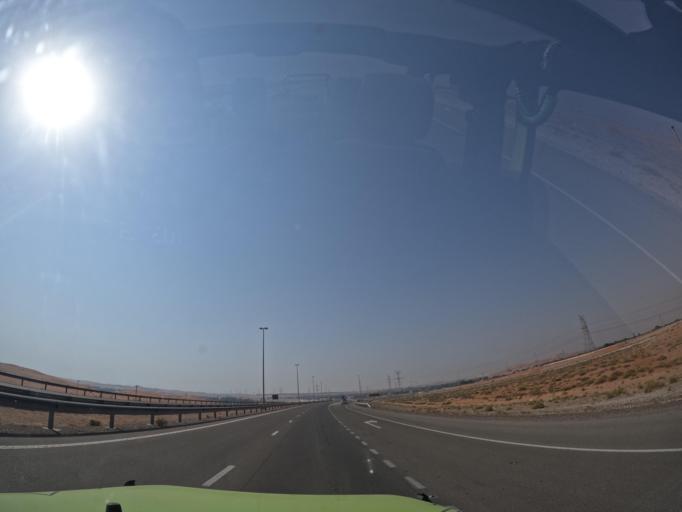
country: OM
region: Al Buraimi
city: Al Buraymi
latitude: 24.3740
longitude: 55.7284
